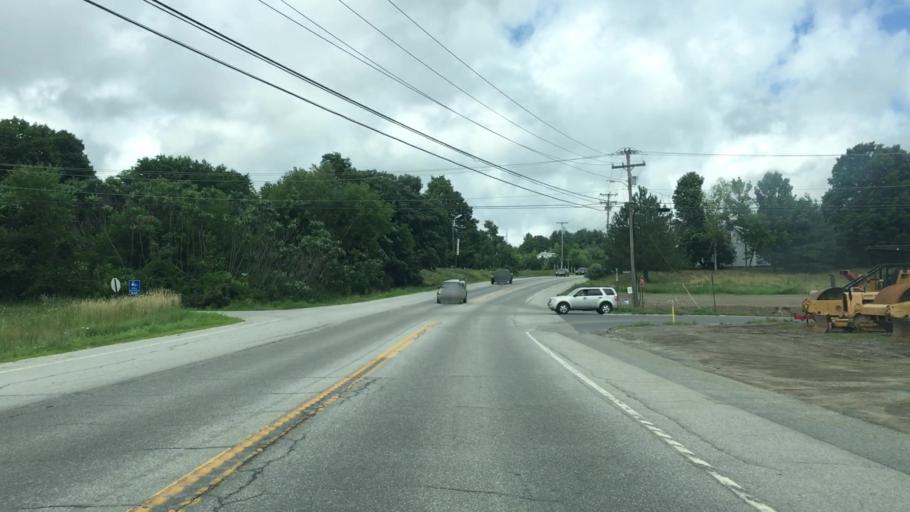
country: US
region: Maine
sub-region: Kennebec County
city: Hallowell
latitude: 44.2849
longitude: -69.7768
